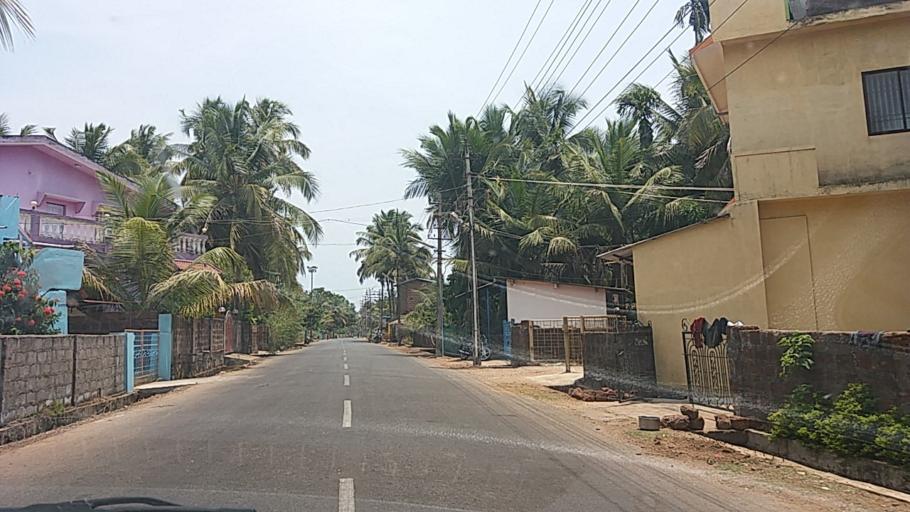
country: IN
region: Karnataka
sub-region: Uttar Kannada
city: Karwar
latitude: 14.8178
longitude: 74.1501
